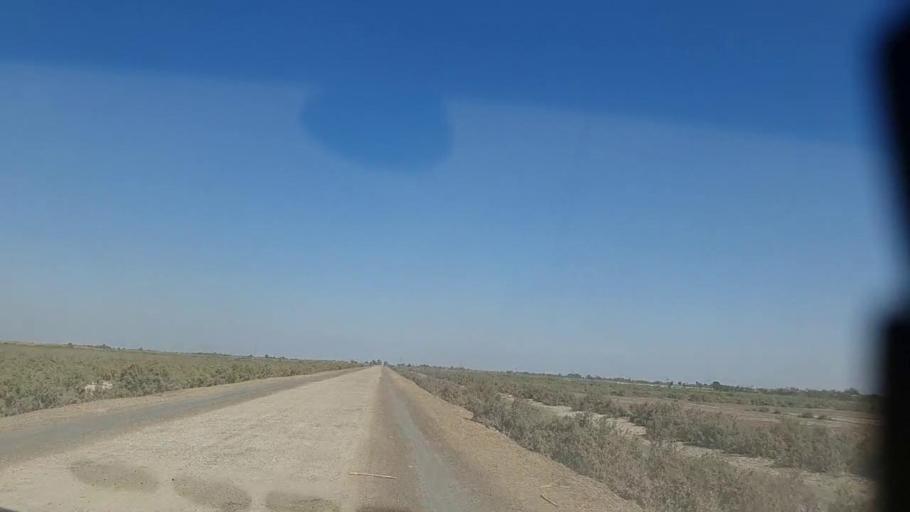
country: PK
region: Sindh
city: Mirwah Gorchani
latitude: 25.2392
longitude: 69.0272
